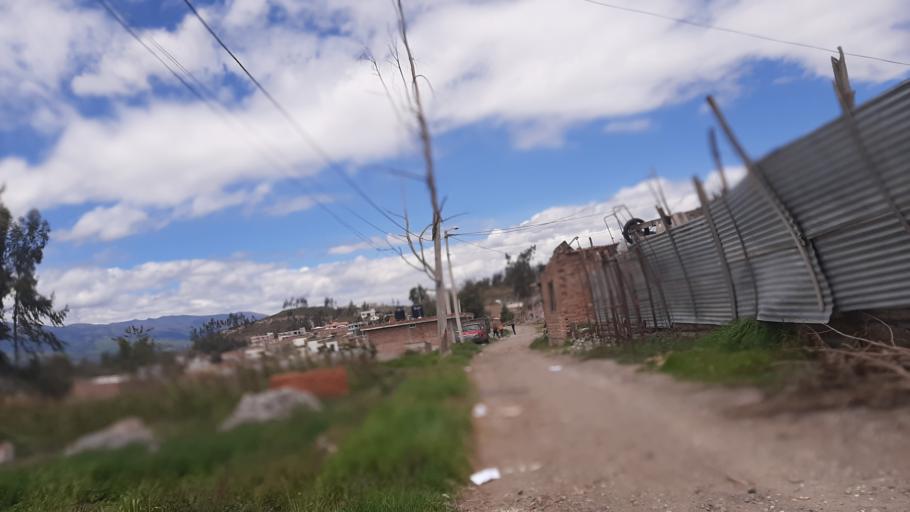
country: EC
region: Chimborazo
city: Riobamba
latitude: -1.6535
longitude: -78.6312
